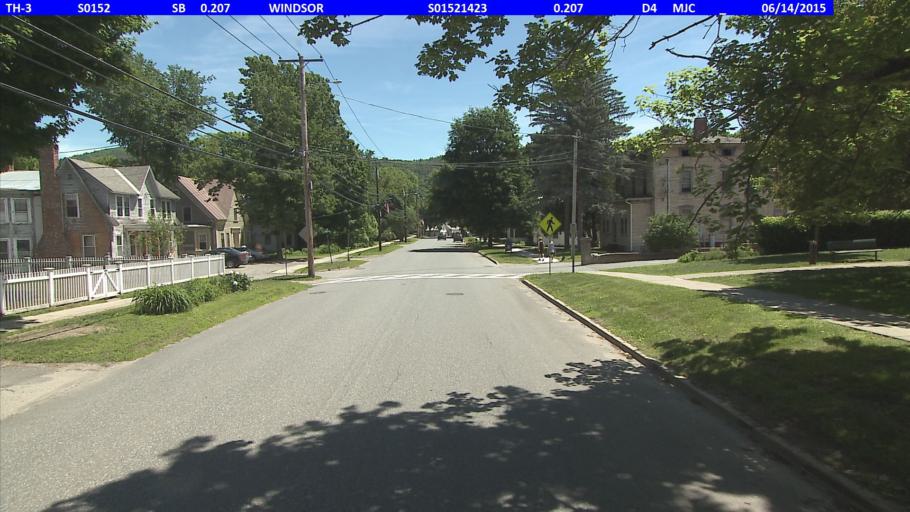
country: US
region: Vermont
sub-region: Windsor County
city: Windsor
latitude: 43.4808
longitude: -72.3903
